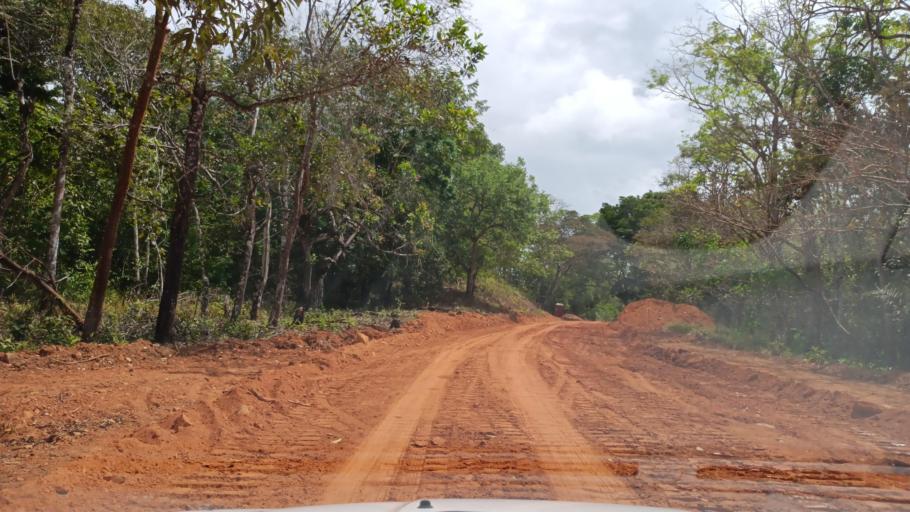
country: PA
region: Panama
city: La Cabima
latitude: 9.1242
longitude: -79.4965
